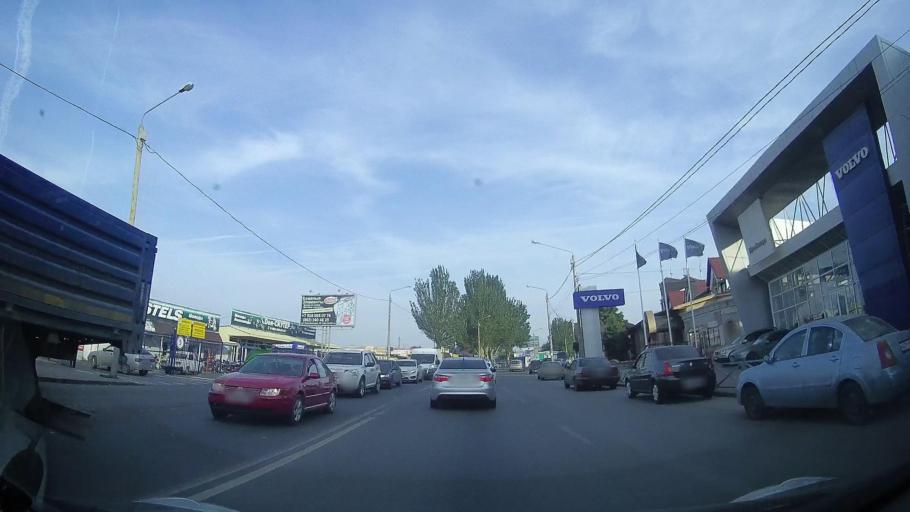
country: RU
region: Rostov
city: Aksay
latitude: 47.2736
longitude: 39.8214
